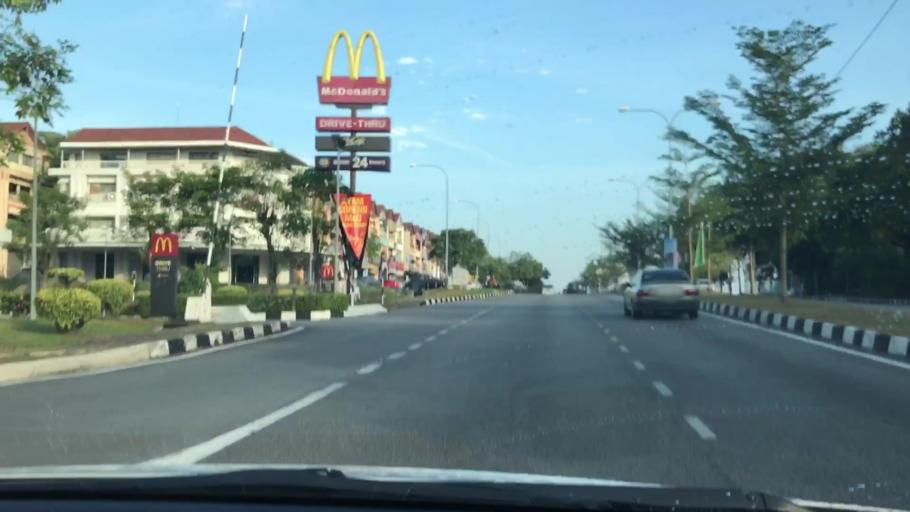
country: MY
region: Putrajaya
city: Putrajaya
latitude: 2.9957
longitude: 101.6710
